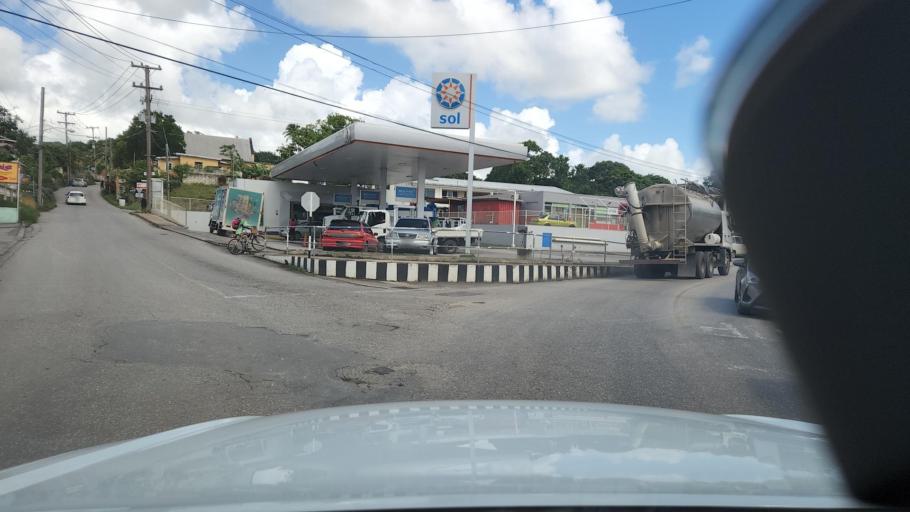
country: BB
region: Saint Thomas
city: Welchman Hall
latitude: 13.1297
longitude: -59.5696
